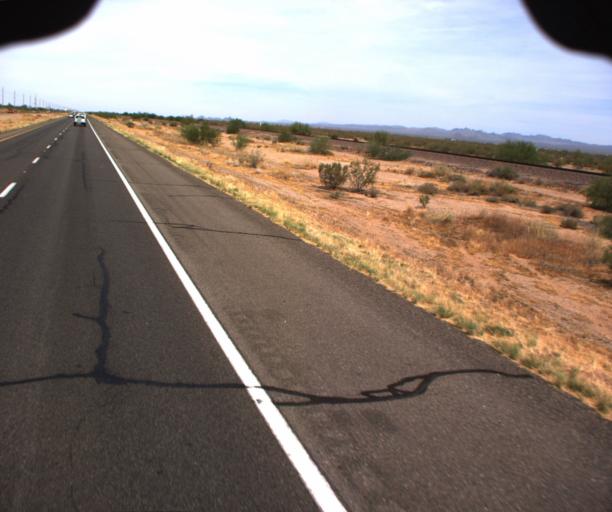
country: US
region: Arizona
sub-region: Maricopa County
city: Sun City West
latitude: 33.7167
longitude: -112.4500
